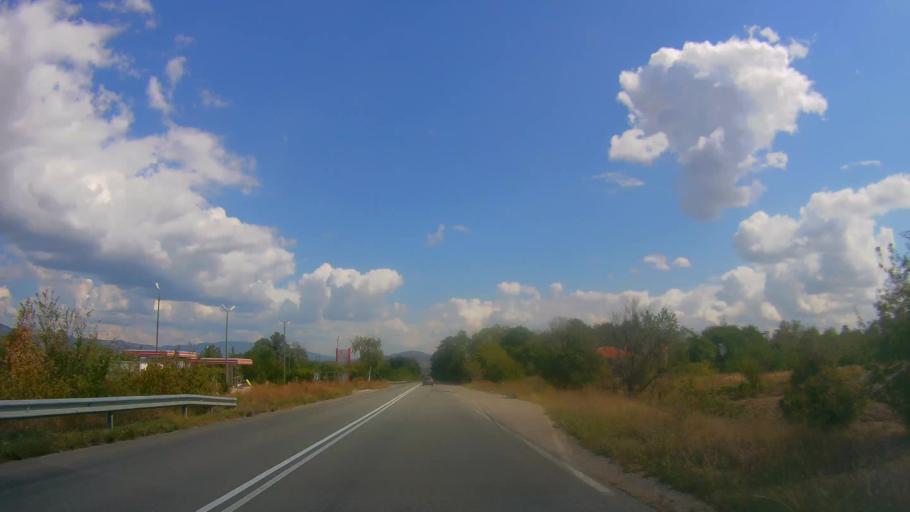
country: BG
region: Sliven
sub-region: Obshtina Tvurditsa
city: Tvurditsa
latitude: 42.6540
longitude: 25.9500
